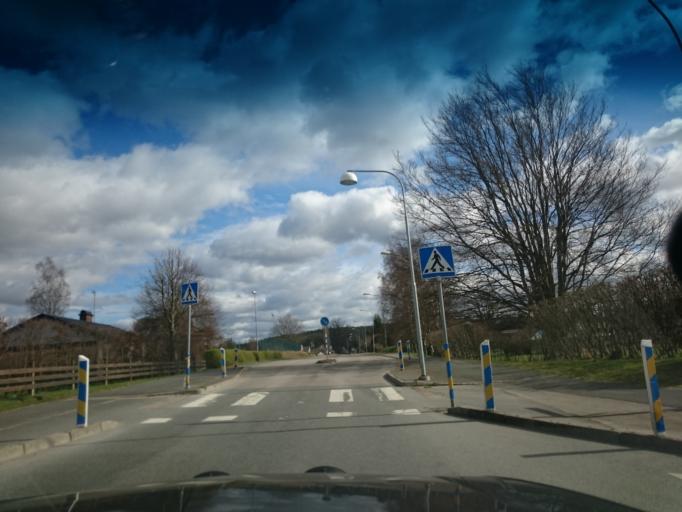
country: SE
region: Joenkoeping
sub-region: Vetlanda Kommun
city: Vetlanda
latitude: 57.4028
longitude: 15.0831
